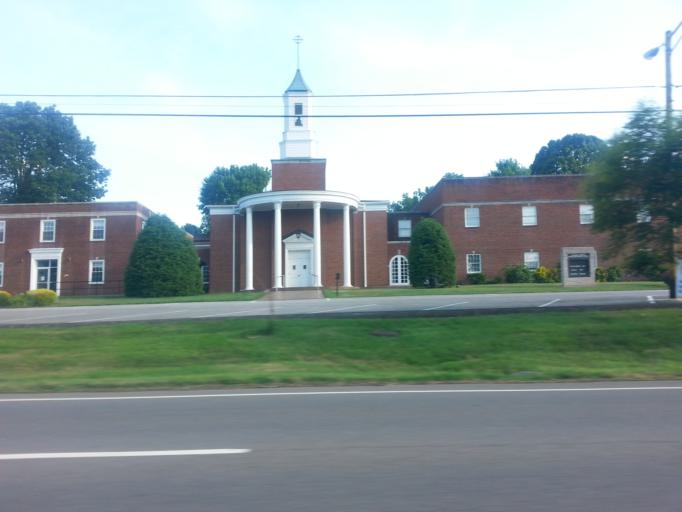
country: US
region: Tennessee
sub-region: Knox County
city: Knoxville
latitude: 35.9212
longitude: -83.8709
